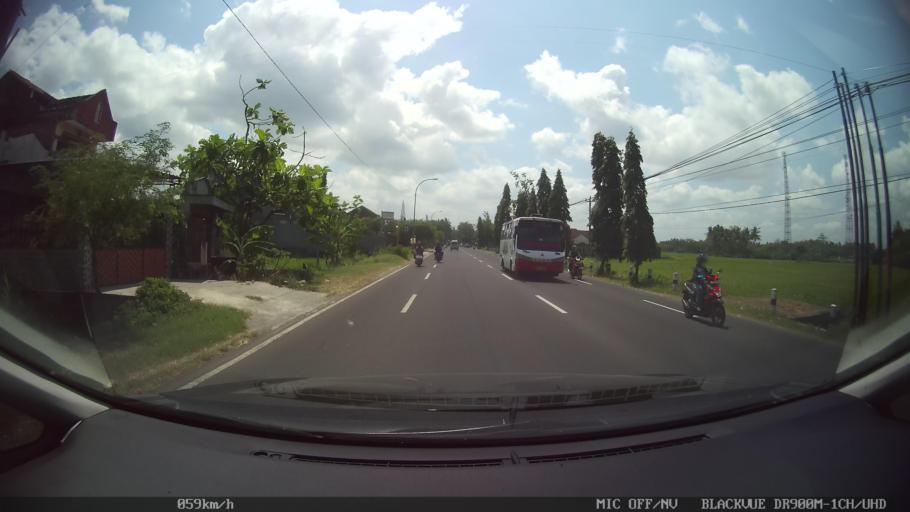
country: ID
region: Daerah Istimewa Yogyakarta
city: Pandak
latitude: -7.9165
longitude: 110.2858
